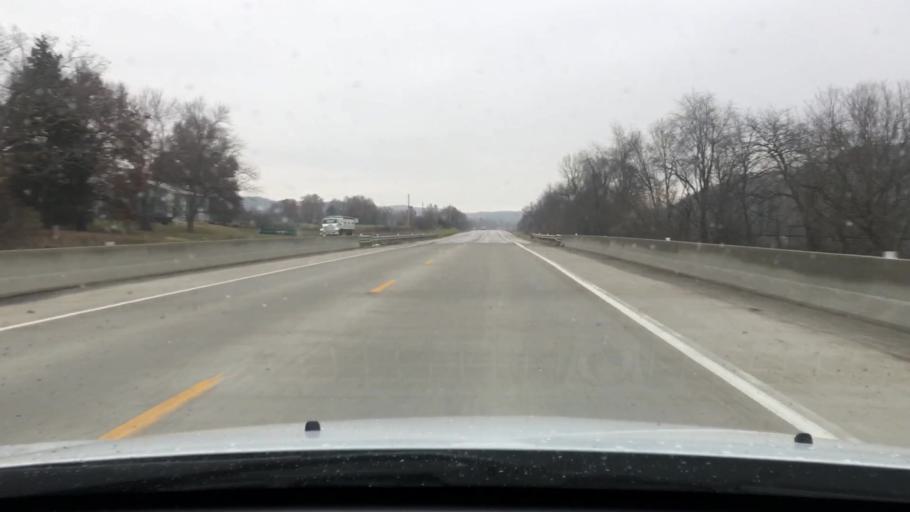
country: US
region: Missouri
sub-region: Pike County
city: Louisiana
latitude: 39.3977
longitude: -91.1115
